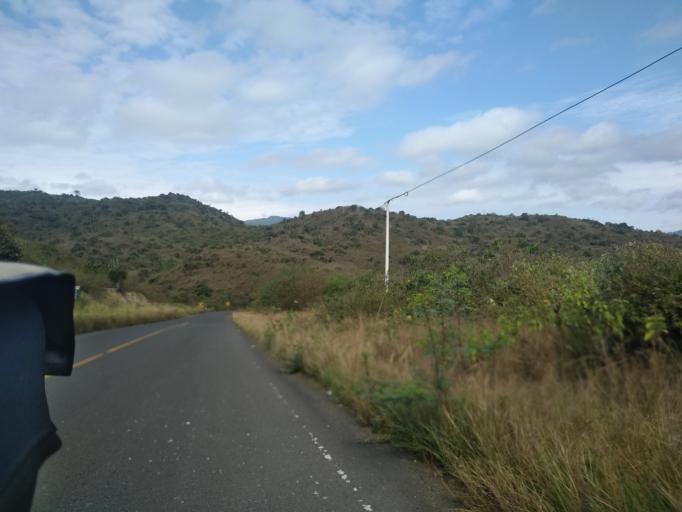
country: EC
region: Manabi
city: Jipijapa
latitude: -1.4390
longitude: -80.7548
